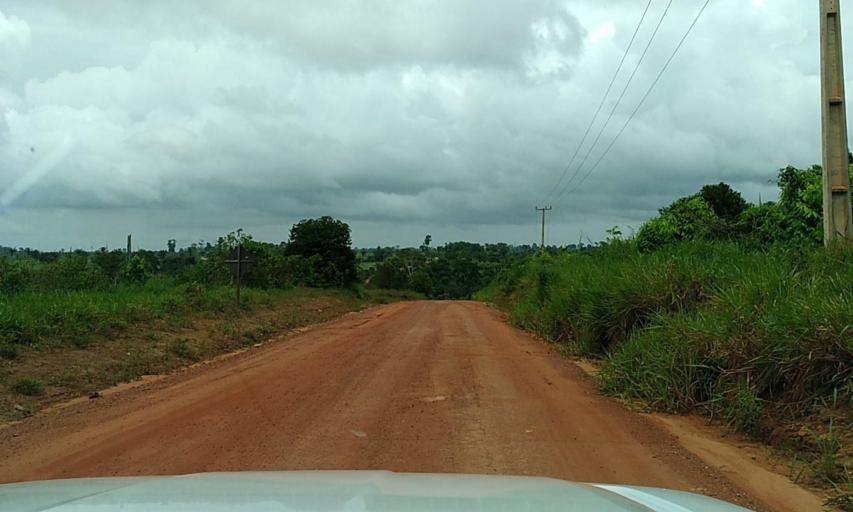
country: BR
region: Para
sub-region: Senador Jose Porfirio
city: Senador Jose Porfirio
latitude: -2.6181
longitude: -51.8674
